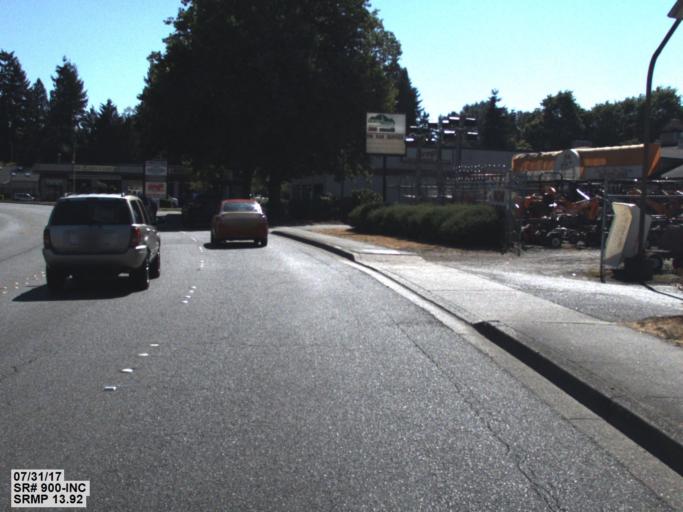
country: US
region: Washington
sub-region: King County
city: Newcastle
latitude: 47.5038
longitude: -122.1643
